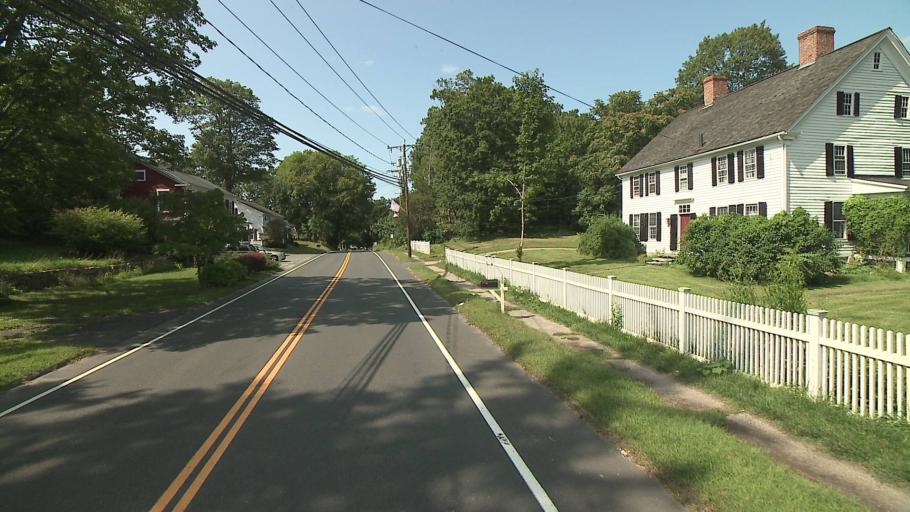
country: US
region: Connecticut
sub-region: Fairfield County
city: Danbury
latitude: 41.4666
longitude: -73.3882
